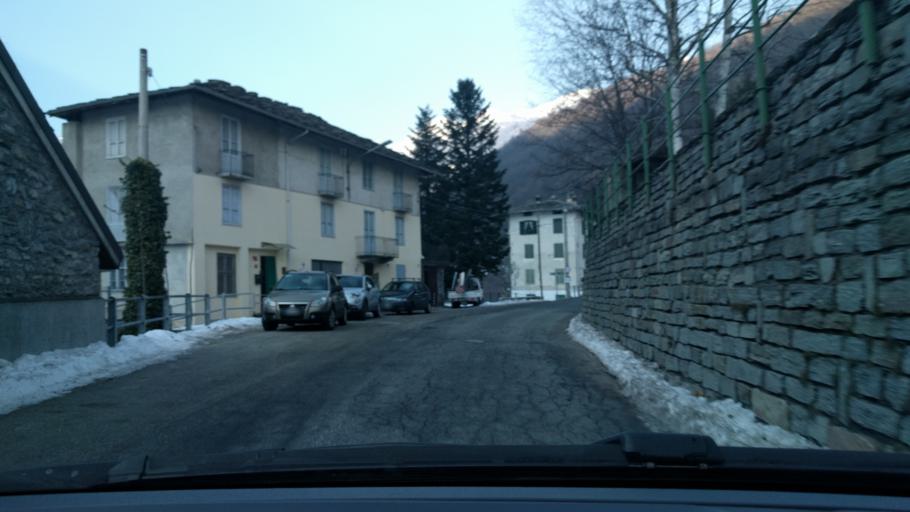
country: IT
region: Piedmont
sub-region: Provincia di Torino
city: Chialamberto
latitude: 45.3681
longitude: 7.3050
